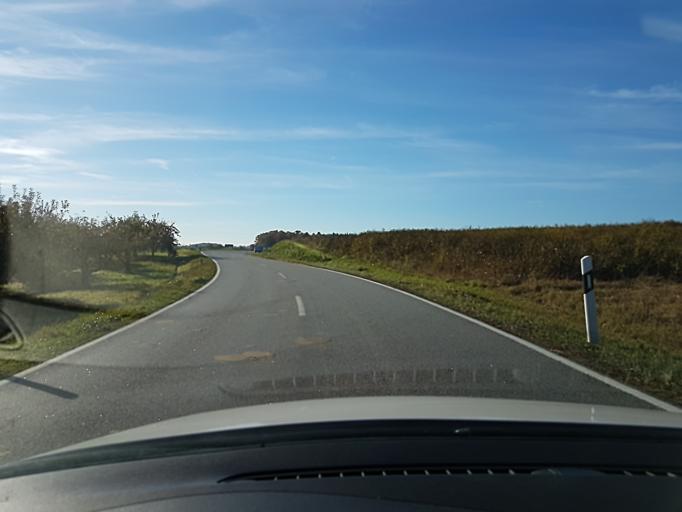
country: DE
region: Baden-Wuerttemberg
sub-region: Karlsruhe Region
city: Billigheim
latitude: 49.3494
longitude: 9.2381
